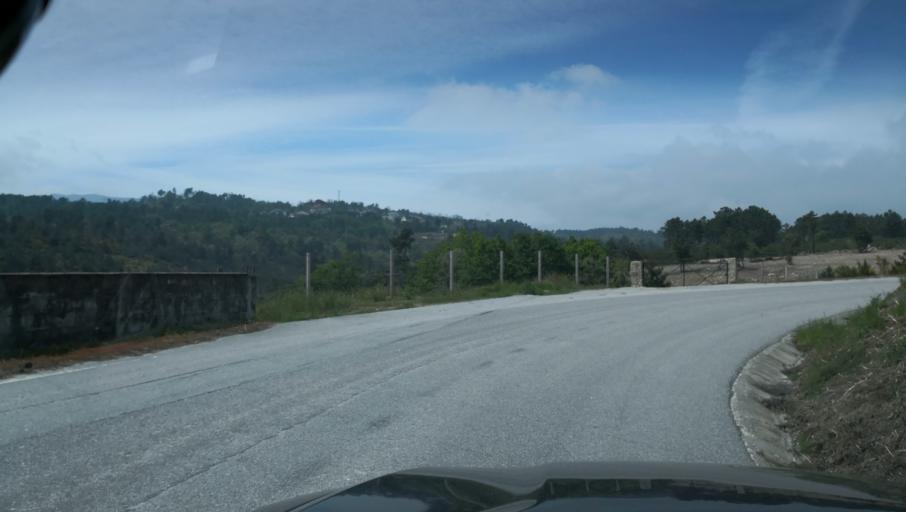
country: PT
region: Vila Real
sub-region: Vila Real
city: Vila Real
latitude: 41.2770
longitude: -7.7993
